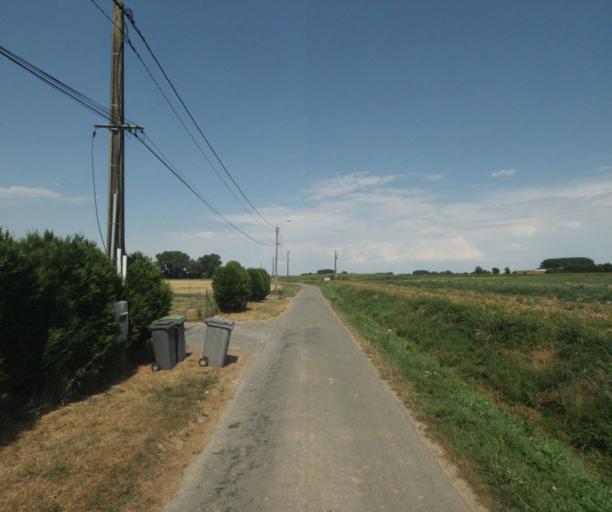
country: FR
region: Nord-Pas-de-Calais
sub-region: Departement du Nord
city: Quesnoy-sur-Deule
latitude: 50.7267
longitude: 2.9883
